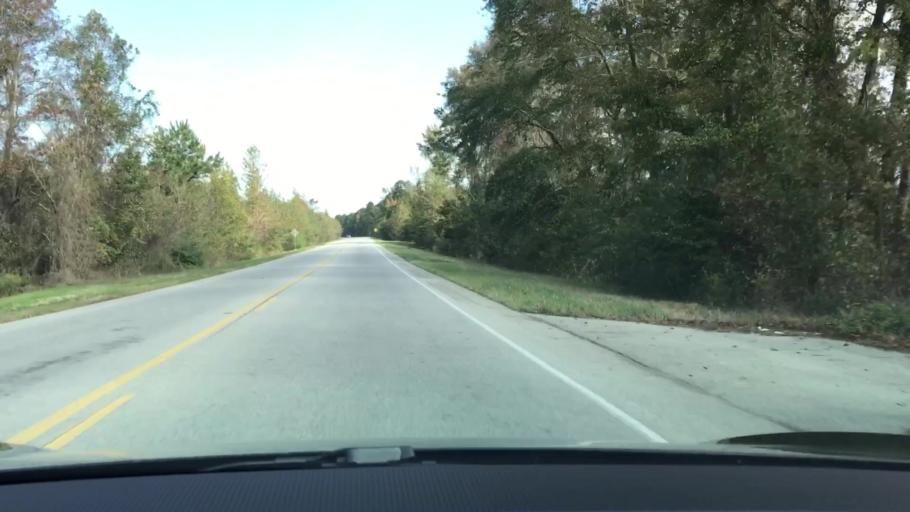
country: US
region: Georgia
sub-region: Jefferson County
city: Louisville
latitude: 32.9534
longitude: -82.3938
